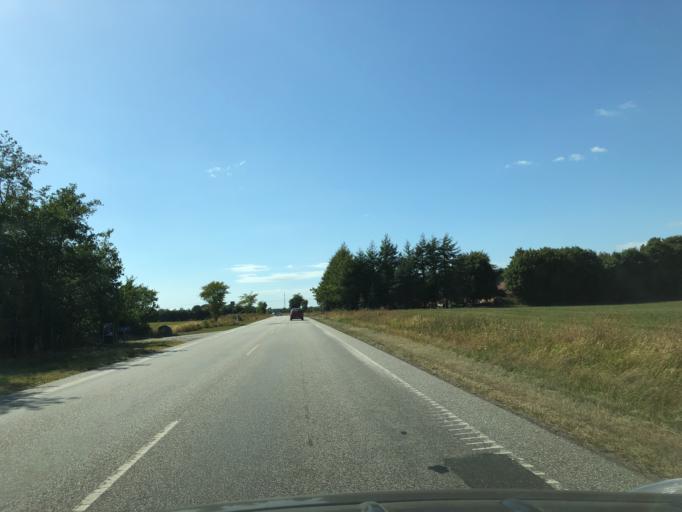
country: DK
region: North Denmark
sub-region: Vesthimmerland Kommune
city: Alestrup
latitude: 56.6192
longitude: 9.5959
